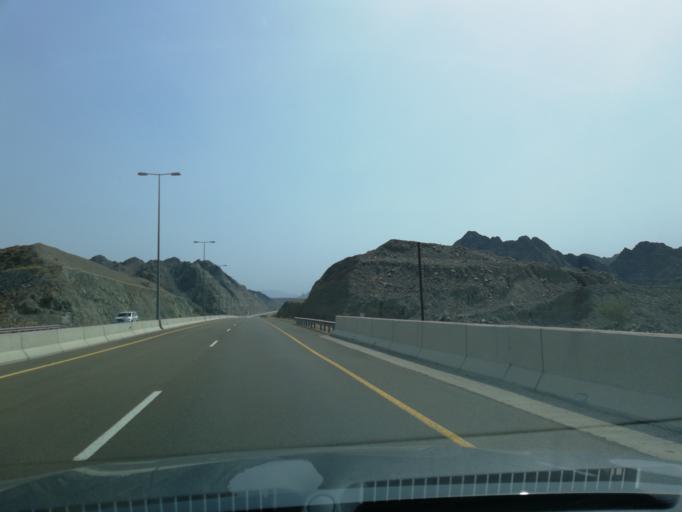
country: OM
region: Al Batinah
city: Al Liwa'
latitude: 24.2706
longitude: 56.3914
